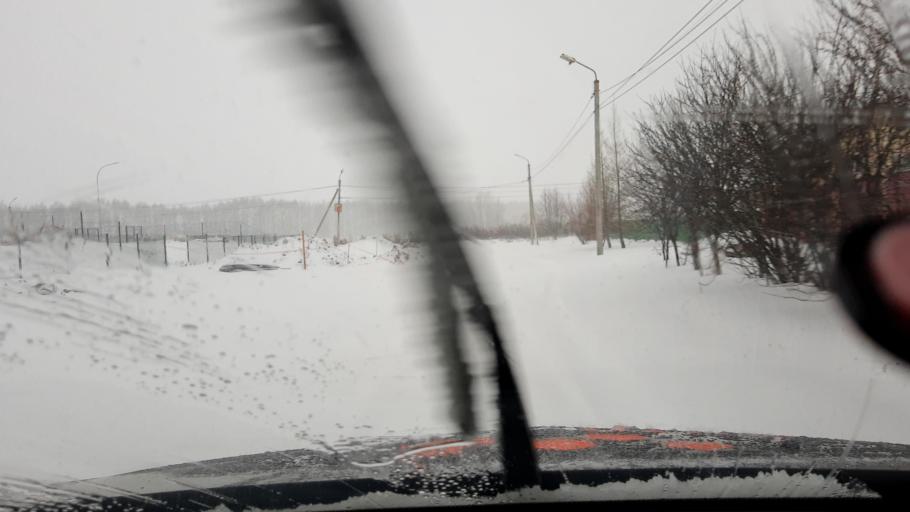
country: RU
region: Bashkortostan
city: Ufa
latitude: 54.8560
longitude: 56.0136
